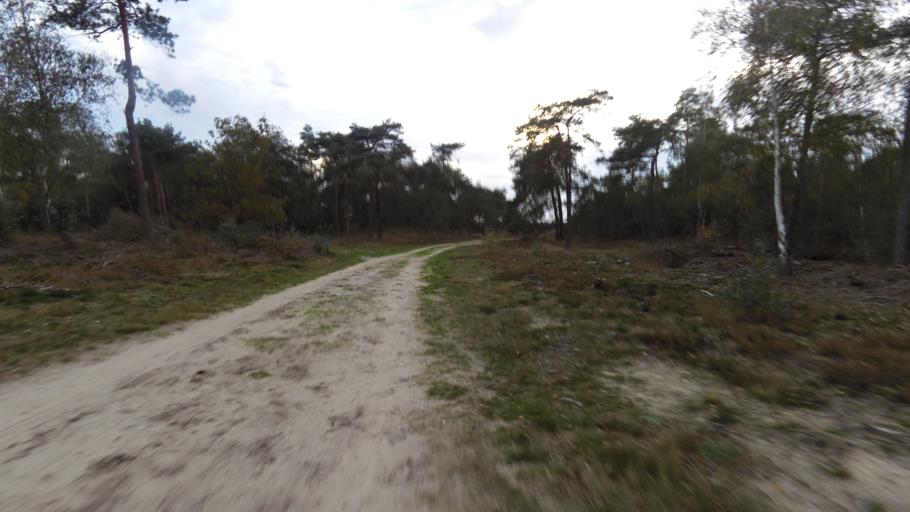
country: NL
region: Gelderland
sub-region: Gemeente Elburg
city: Elburg
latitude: 52.3956
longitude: 5.8531
